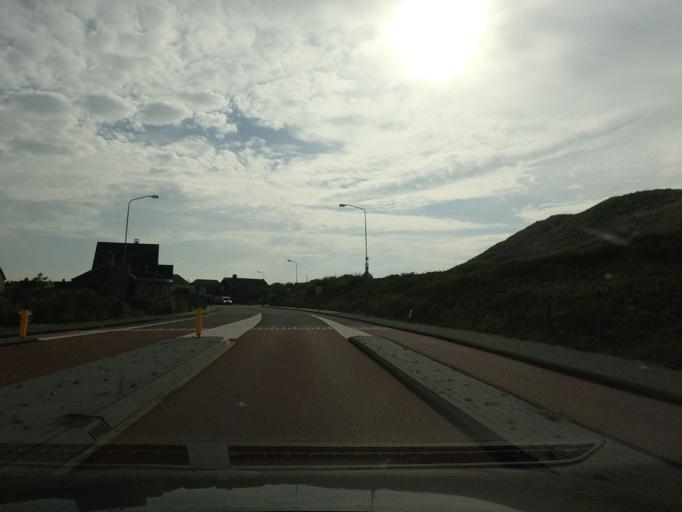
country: NL
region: North Holland
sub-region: Gemeente Schagen
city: Schagen
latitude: 52.8396
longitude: 4.6945
